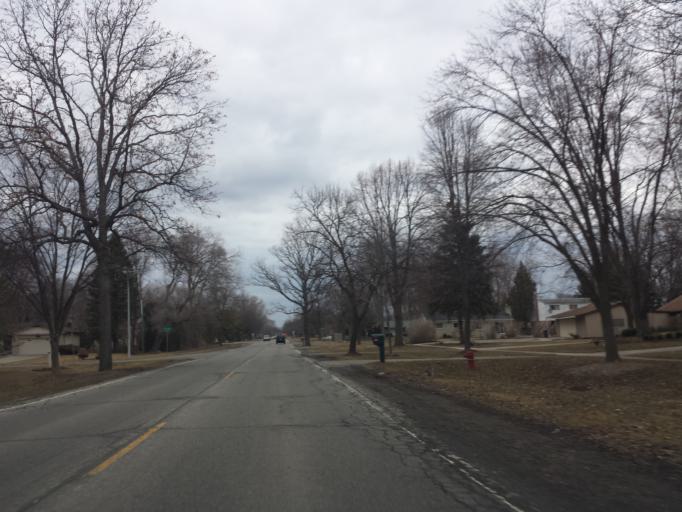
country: US
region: Michigan
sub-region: Oakland County
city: Lathrup Village
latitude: 42.5071
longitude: -83.2421
